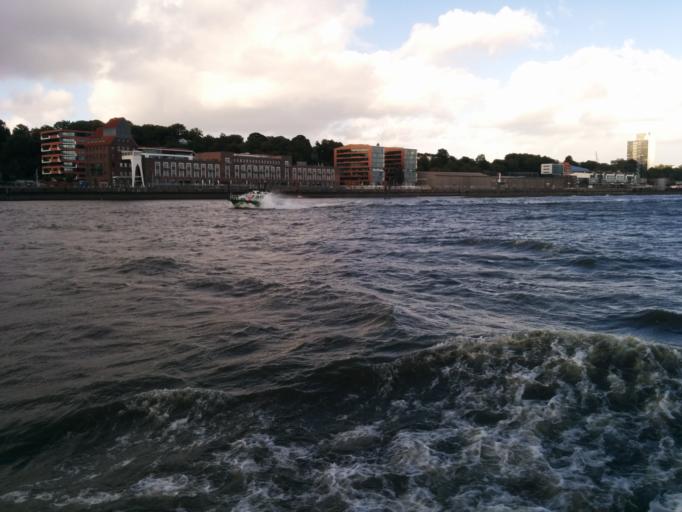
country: DE
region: Hamburg
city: Altona
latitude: 53.5413
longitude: 9.9236
